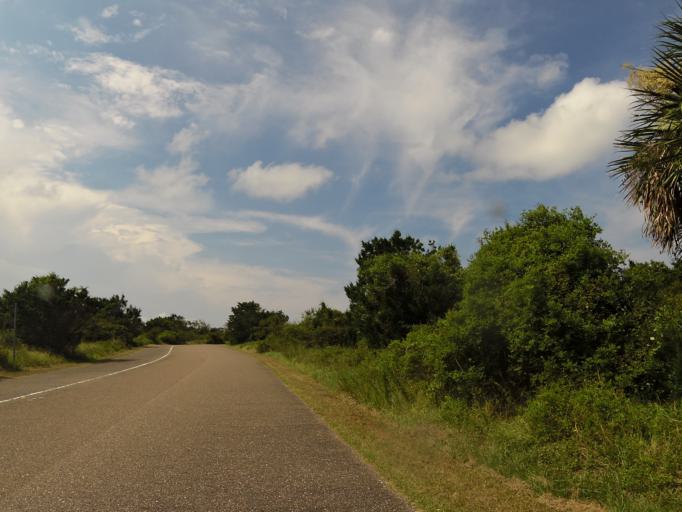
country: US
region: Florida
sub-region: Duval County
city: Atlantic Beach
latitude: 30.4462
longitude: -81.4140
